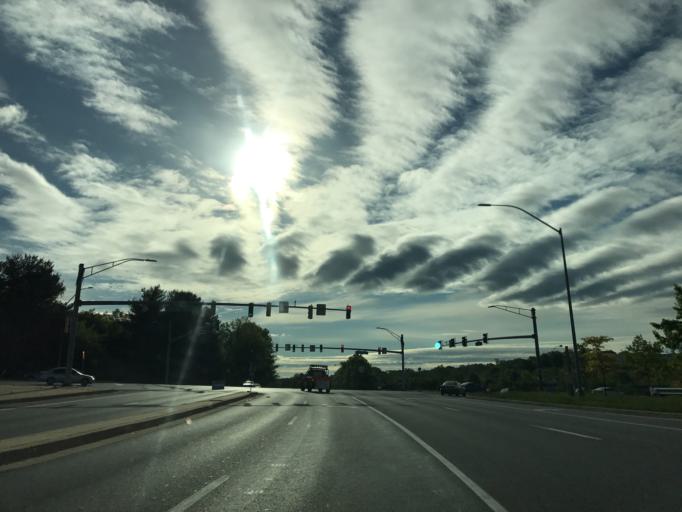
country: US
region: Maryland
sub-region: Baltimore County
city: Owings Mills
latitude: 39.4038
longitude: -76.7970
